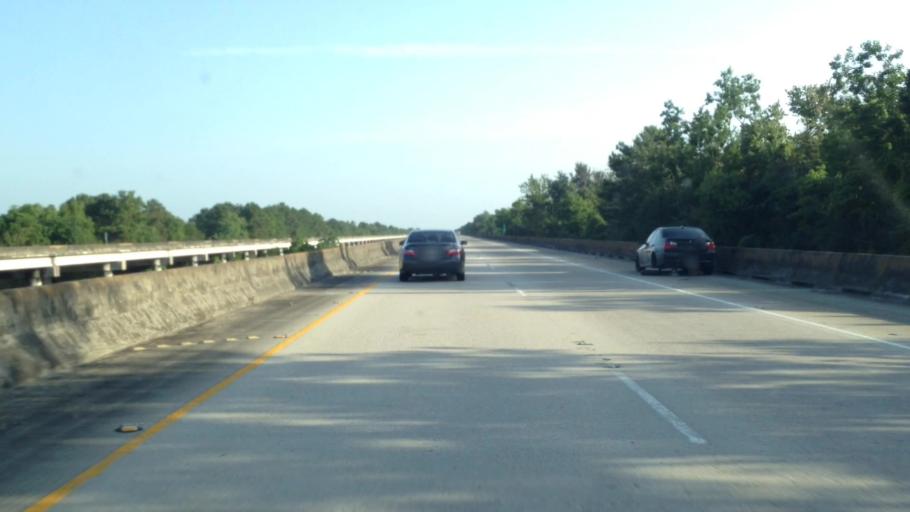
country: US
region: Louisiana
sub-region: Tangipahoa Parish
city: Ponchatoula
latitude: 30.3568
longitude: -90.4178
